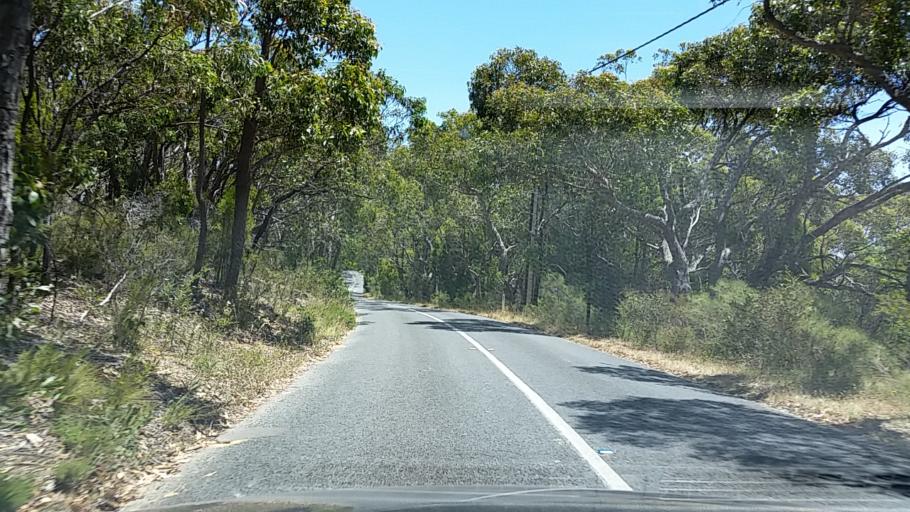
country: AU
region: South Australia
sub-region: Adelaide Hills
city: Crafers
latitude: -34.9890
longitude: 138.6856
